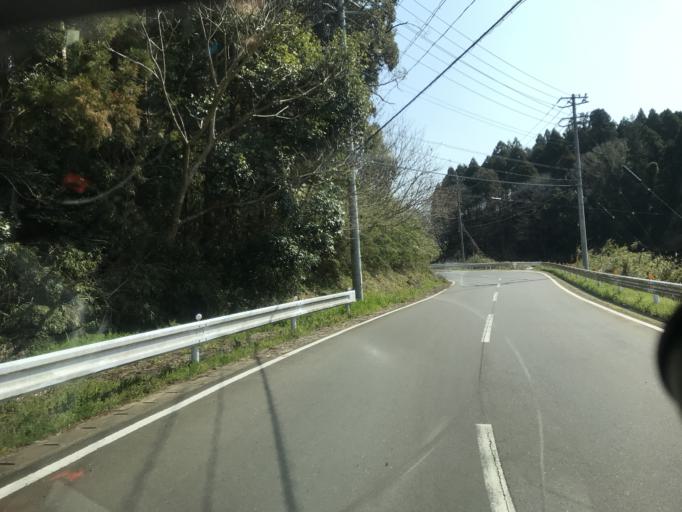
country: JP
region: Chiba
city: Sawara
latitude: 35.8534
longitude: 140.5525
